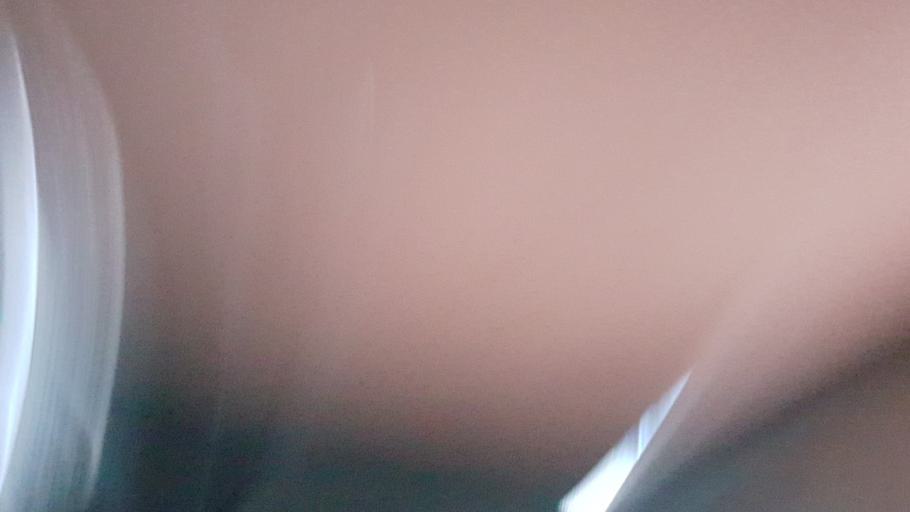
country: TH
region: Mae Hong Son
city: Pa Pae
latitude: 18.2452
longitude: 97.9421
